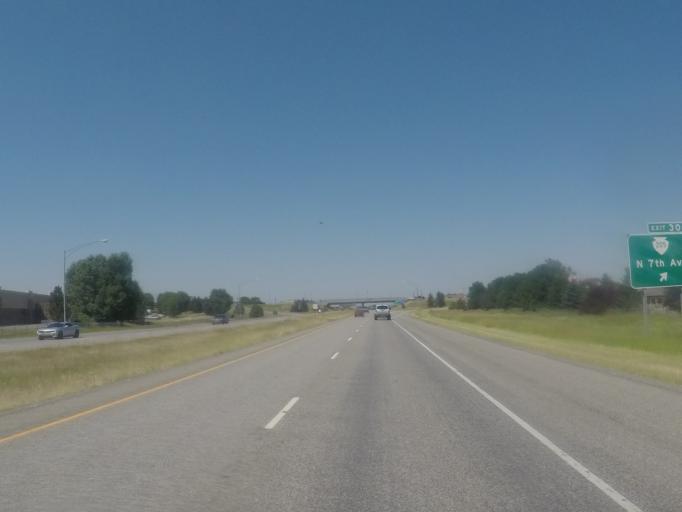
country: US
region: Montana
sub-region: Gallatin County
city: Bozeman
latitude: 45.6958
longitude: -111.0399
